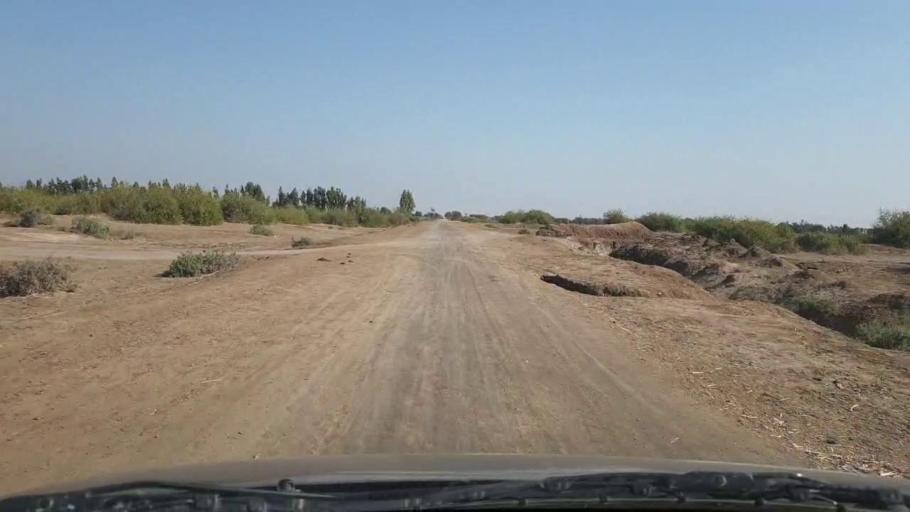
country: PK
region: Sindh
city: Samaro
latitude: 25.1946
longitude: 69.2784
